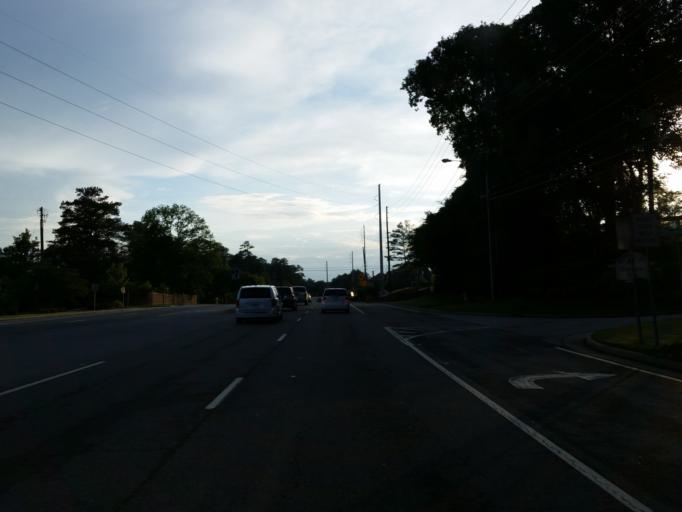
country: US
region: Georgia
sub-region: Fulton County
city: Roswell
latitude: 34.0019
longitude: -84.3980
